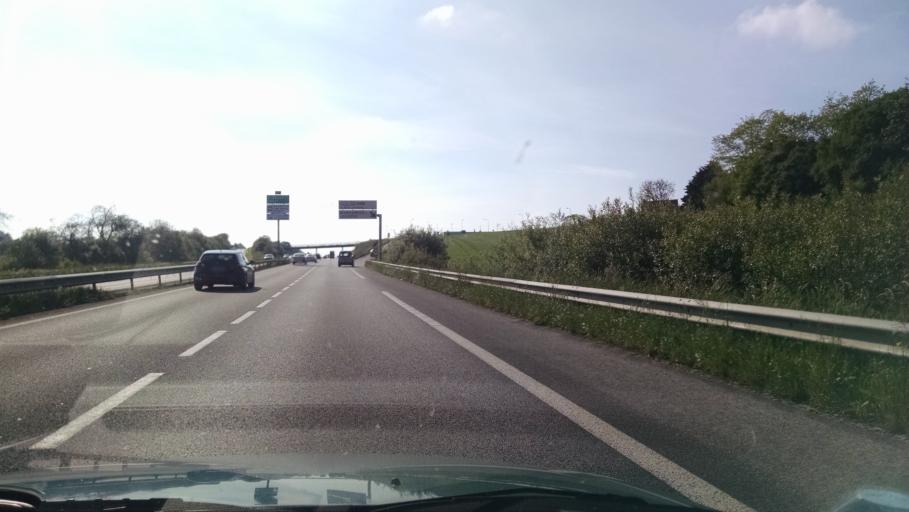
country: FR
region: Brittany
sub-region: Departement des Cotes-d'Armor
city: Lamballe
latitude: 48.4587
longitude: -2.5266
